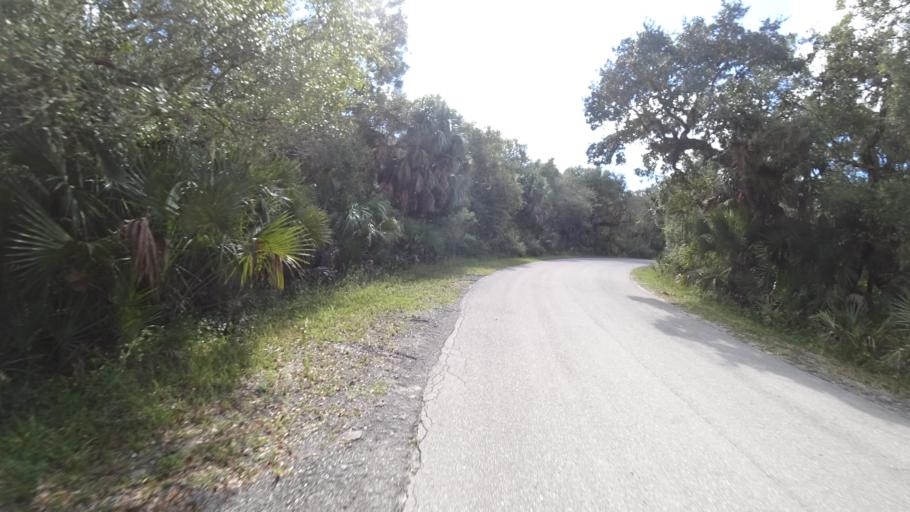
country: US
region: Florida
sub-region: Sarasota County
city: Lake Sarasota
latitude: 27.2864
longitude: -82.2534
